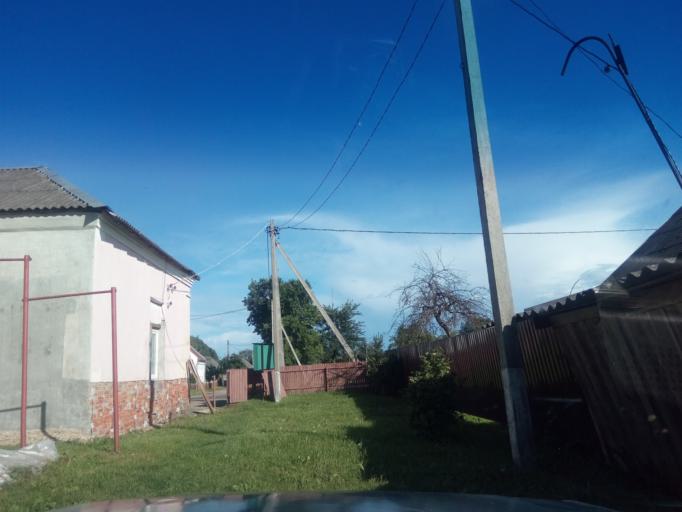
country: BY
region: Vitebsk
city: Dzisna
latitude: 55.6684
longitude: 28.3281
